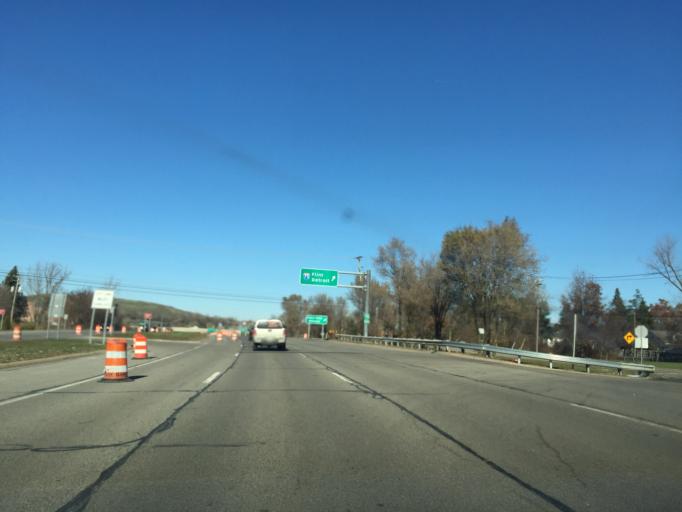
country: US
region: Michigan
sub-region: Oakland County
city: Auburn Hills
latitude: 42.6884
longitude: -83.2408
